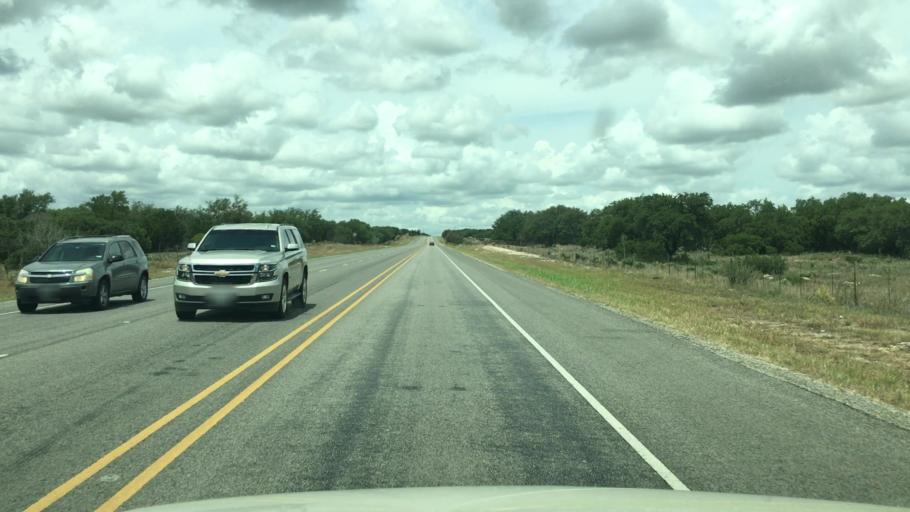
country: US
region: Texas
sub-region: McCulloch County
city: Brady
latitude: 31.0281
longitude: -99.2259
